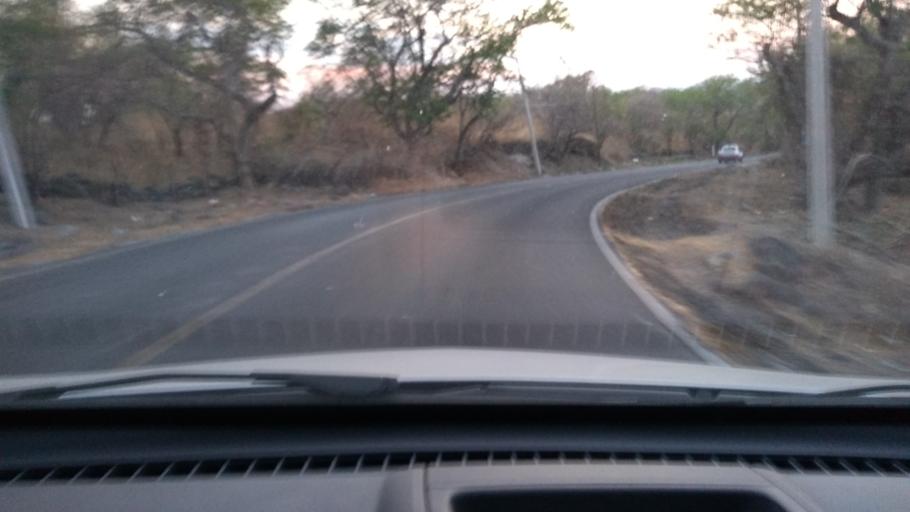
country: MX
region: Morelos
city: Coatetelco
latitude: 18.7214
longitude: -99.3084
